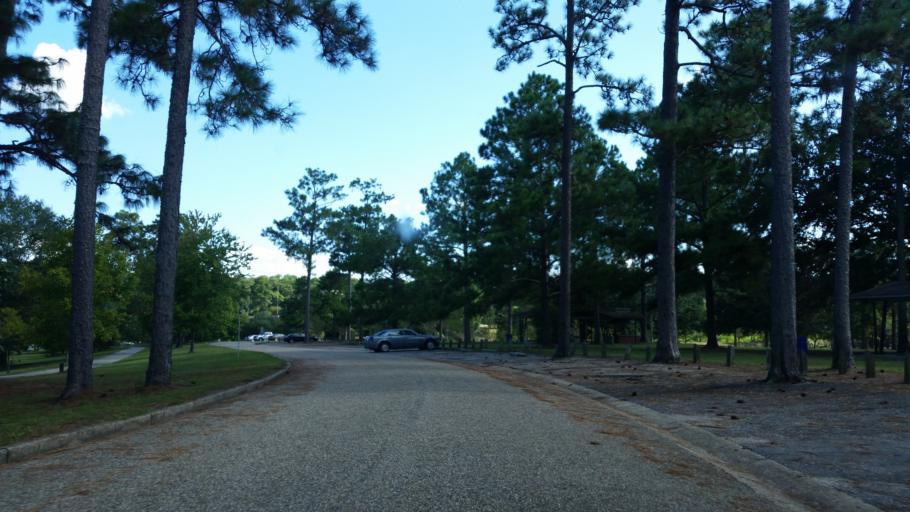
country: US
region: Alabama
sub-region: Mobile County
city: Prichard
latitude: 30.7082
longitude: -88.1550
